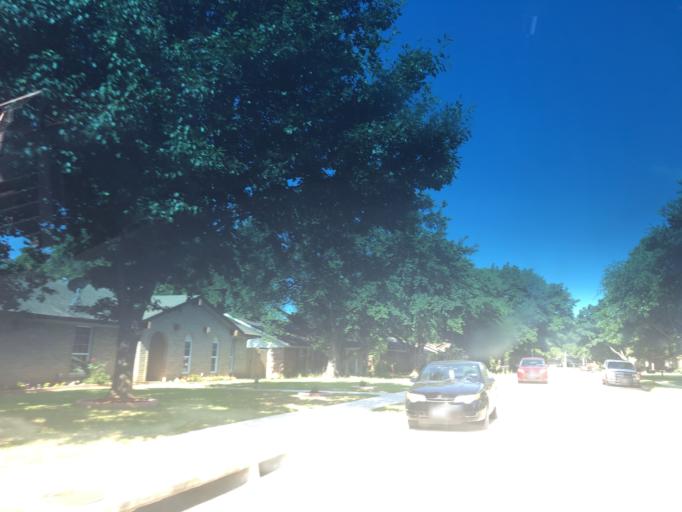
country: US
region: Texas
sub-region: Dallas County
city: Grand Prairie
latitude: 32.7155
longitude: -97.0152
